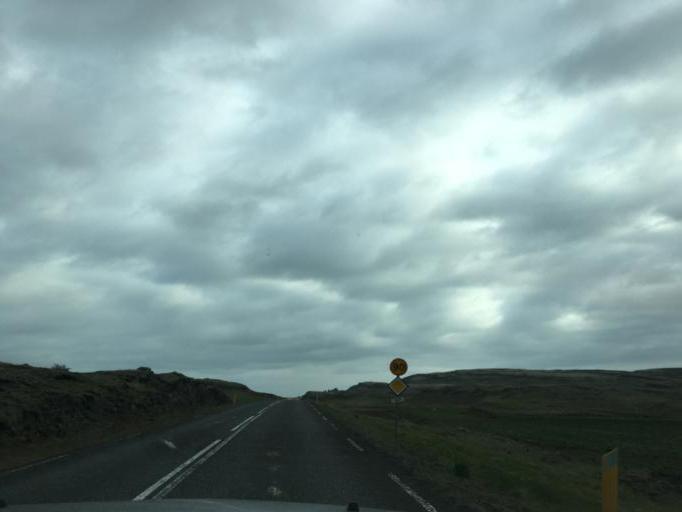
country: IS
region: South
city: Vestmannaeyjar
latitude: 64.2085
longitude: -20.2697
